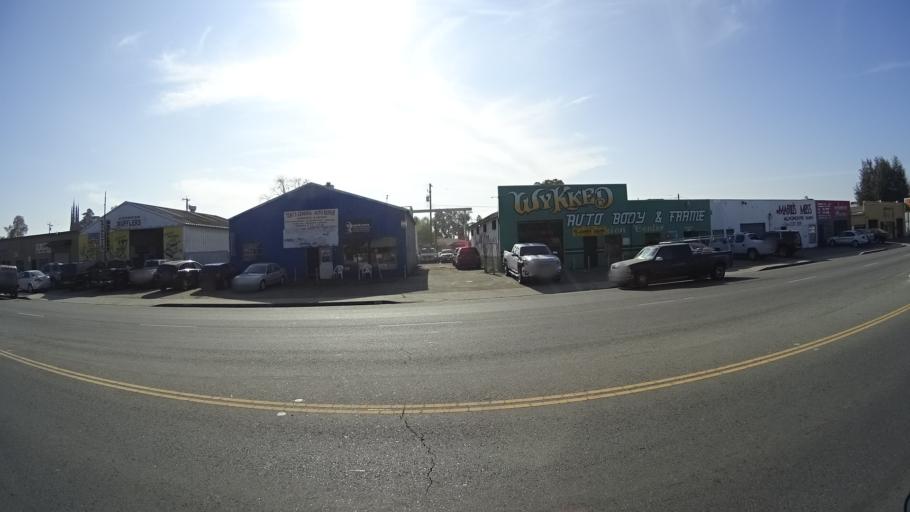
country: US
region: California
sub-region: Kern County
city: Bakersfield
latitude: 35.3539
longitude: -119.0003
